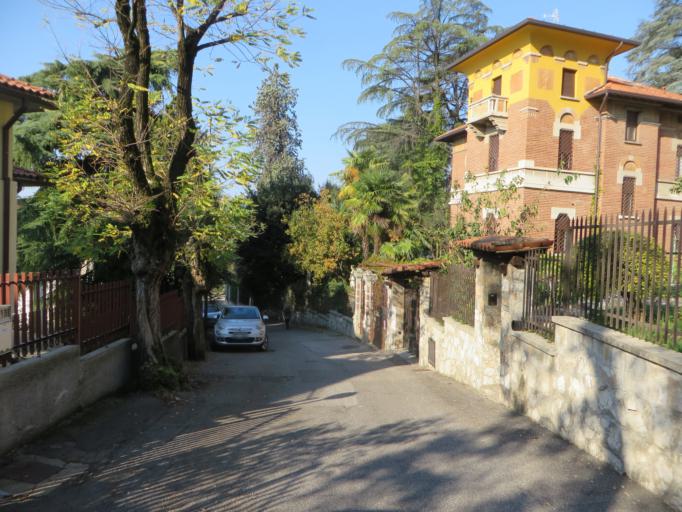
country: IT
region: Lombardy
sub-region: Provincia di Brescia
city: Brescia
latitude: 45.5400
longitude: 10.2358
